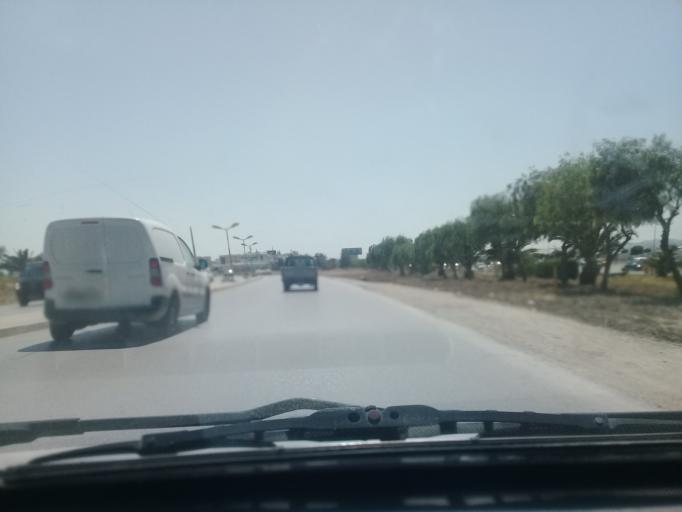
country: TN
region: Tunis
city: La Goulette
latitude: 36.8439
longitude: 10.2523
